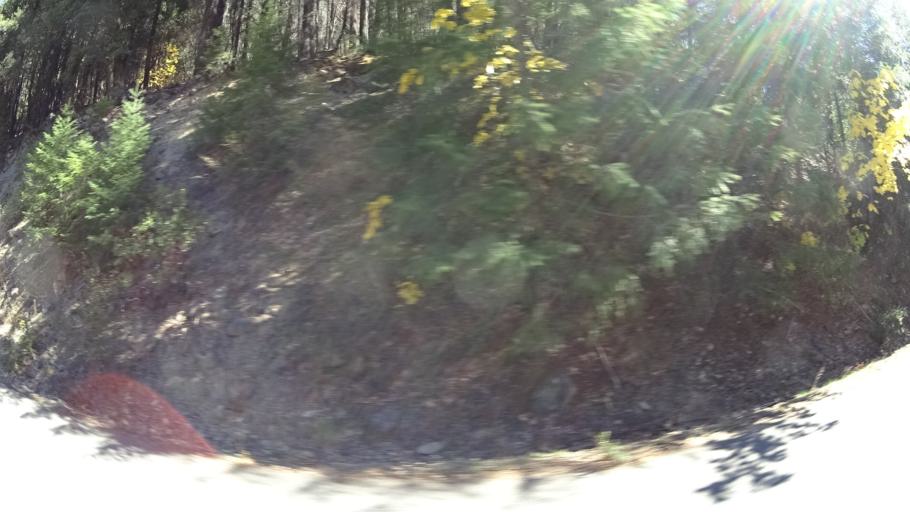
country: US
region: California
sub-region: Siskiyou County
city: Happy Camp
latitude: 41.3485
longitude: -123.0415
